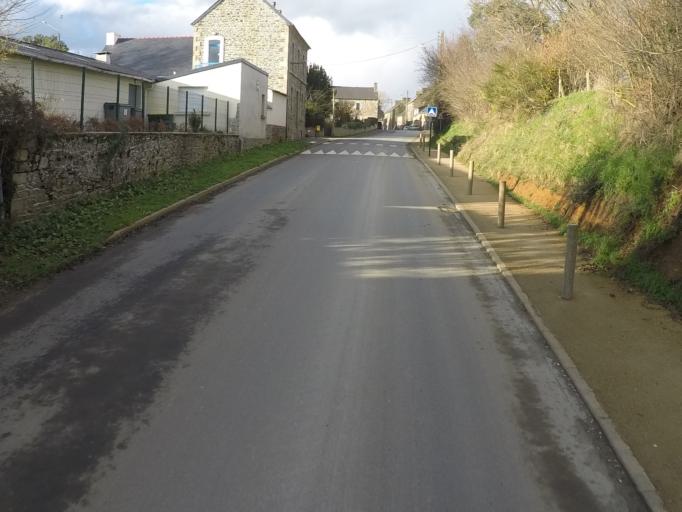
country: FR
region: Brittany
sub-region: Departement des Cotes-d'Armor
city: Lanvollon
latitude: 48.6153
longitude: -2.9837
